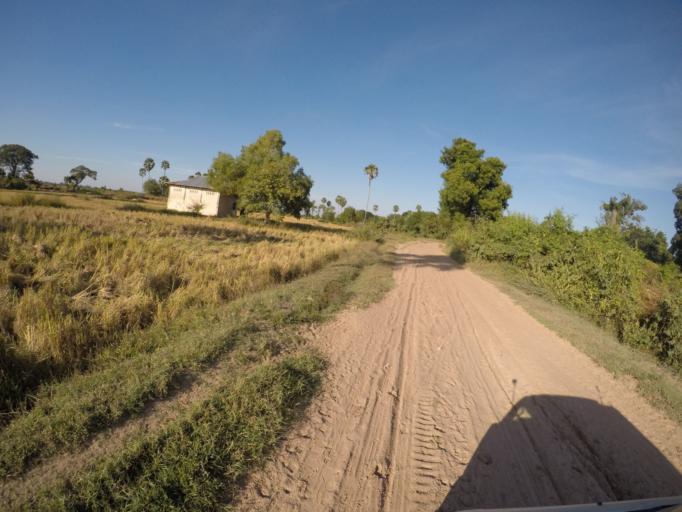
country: MM
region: Bago
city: Pyay
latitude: 18.7948
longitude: 95.3060
